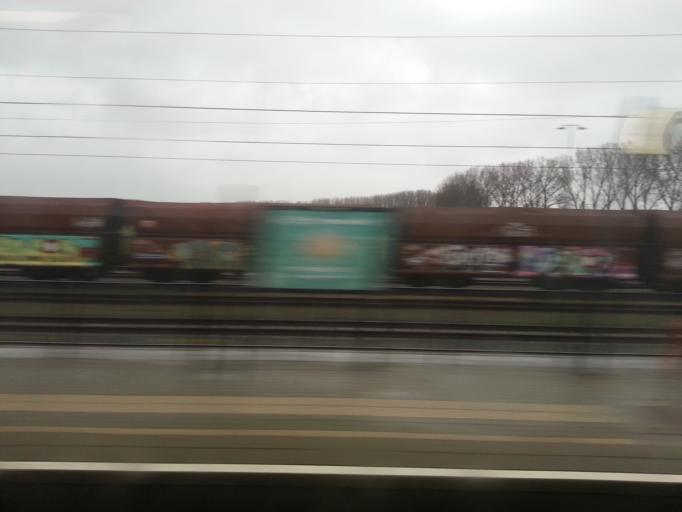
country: NL
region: South Holland
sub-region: Gemeente Dordrecht
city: Dordrecht
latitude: 51.6910
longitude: 4.6631
